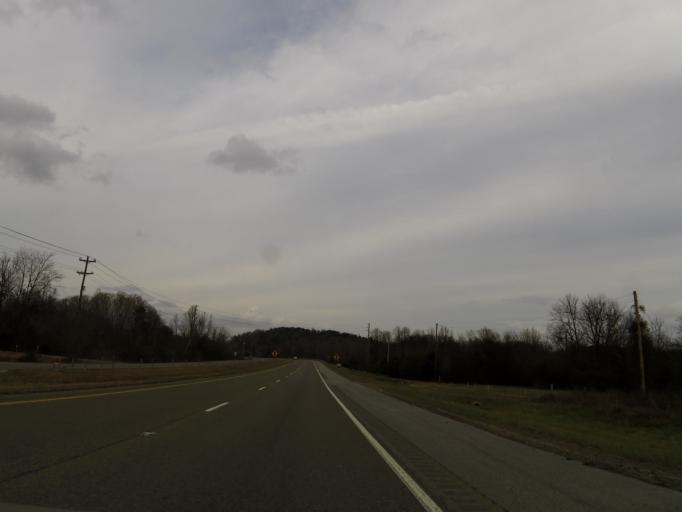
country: US
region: Tennessee
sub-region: Hamilton County
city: Sale Creek
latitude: 35.3333
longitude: -85.1305
